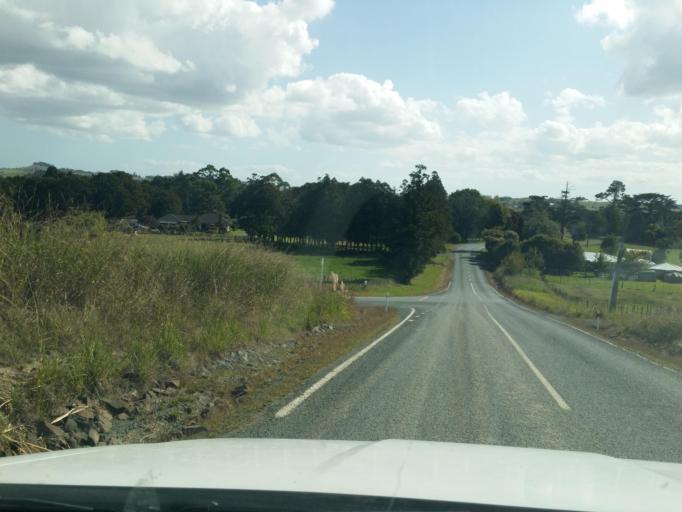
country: NZ
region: Auckland
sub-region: Auckland
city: Wellsford
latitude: -36.1500
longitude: 174.5151
